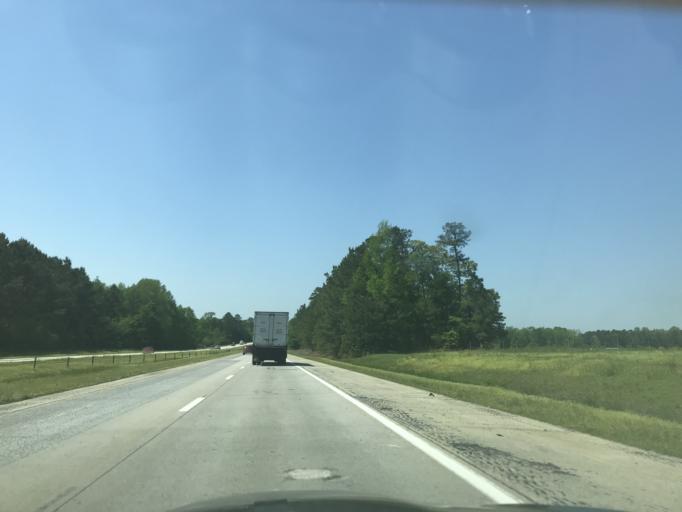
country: US
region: North Carolina
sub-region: Johnston County
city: Benson
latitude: 35.3793
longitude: -78.5073
